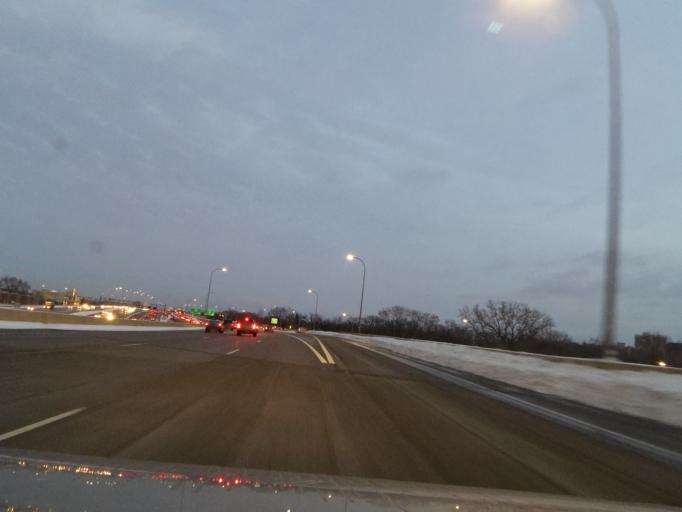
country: US
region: Minnesota
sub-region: Hennepin County
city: Richfield
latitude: 44.8900
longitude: -93.2950
